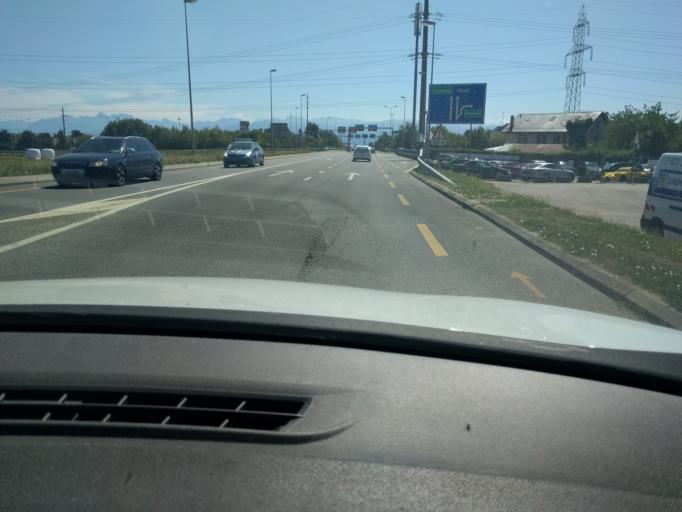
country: CH
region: Vaud
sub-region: Nyon District
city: Gland
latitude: 46.4258
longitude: 6.2554
